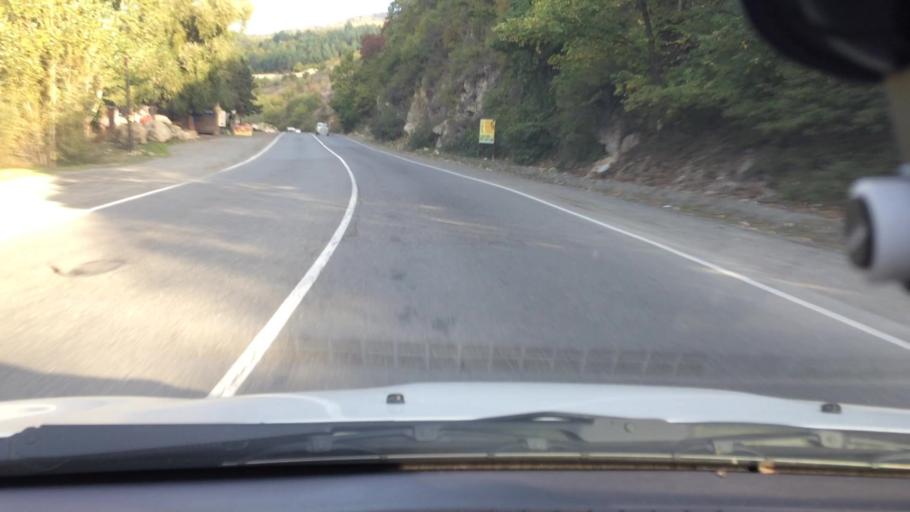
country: GE
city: Surami
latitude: 42.0359
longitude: 43.5201
